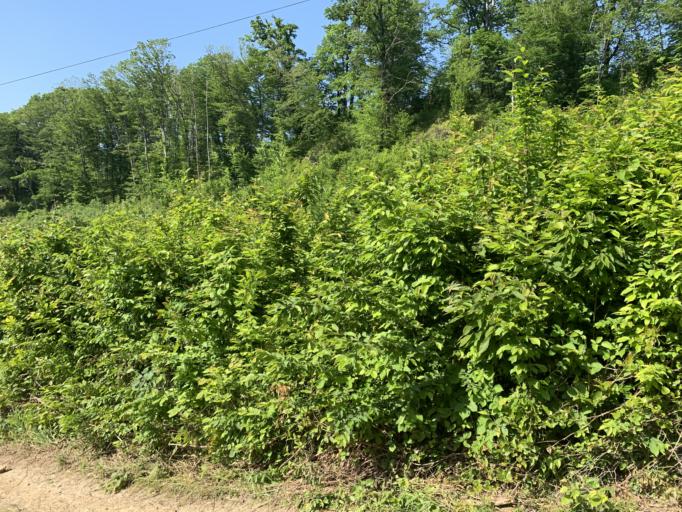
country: RU
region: Krasnodarskiy
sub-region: Sochi City
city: Lazarevskoye
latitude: 43.9510
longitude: 39.3196
